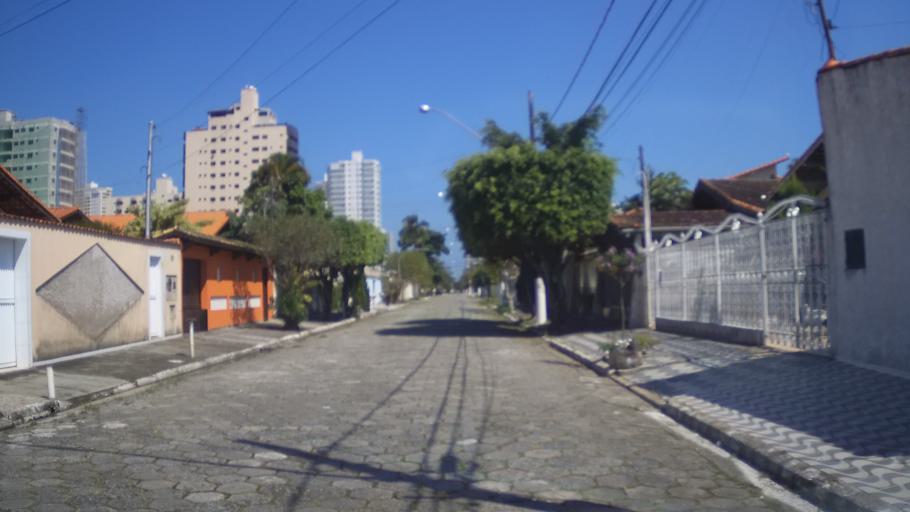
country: BR
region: Sao Paulo
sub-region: Praia Grande
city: Praia Grande
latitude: -24.0089
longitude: -46.4027
